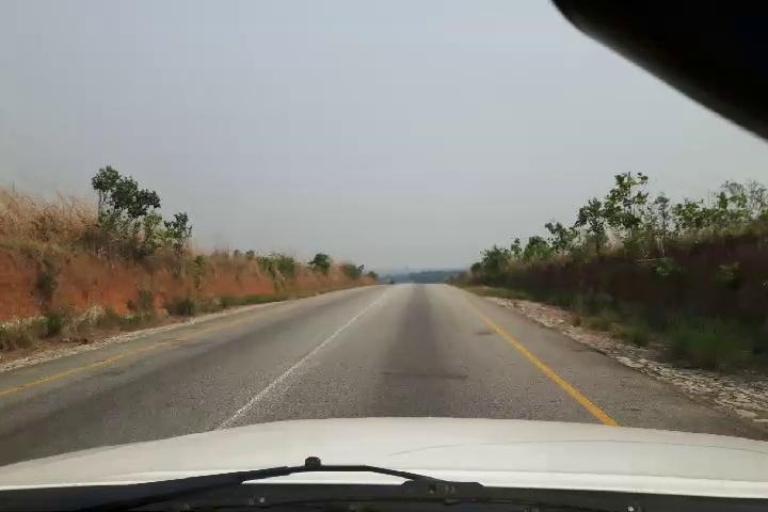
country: SL
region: Southern Province
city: Largo
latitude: 8.2277
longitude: -12.0776
